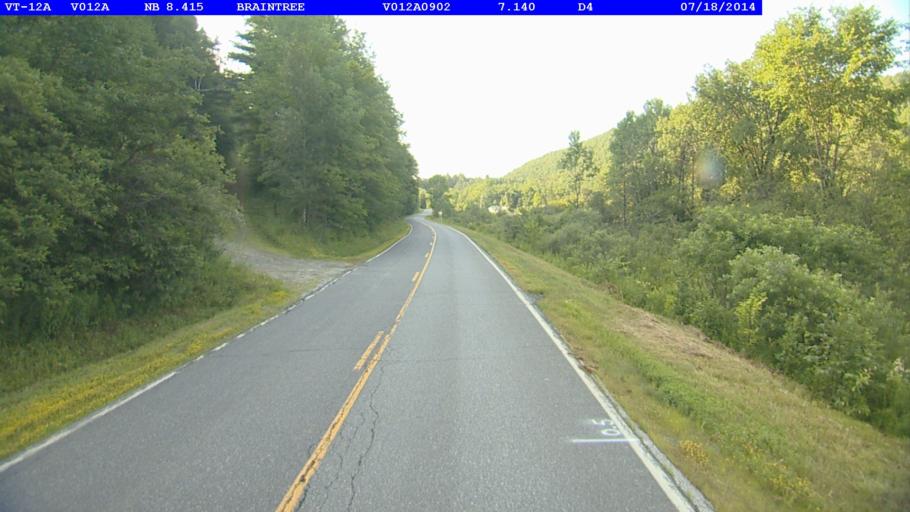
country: US
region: Vermont
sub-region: Orange County
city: Randolph
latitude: 44.0100
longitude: -72.7549
